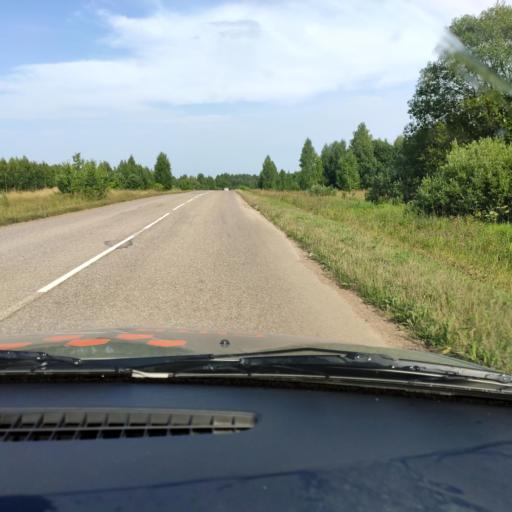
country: RU
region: Bashkortostan
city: Pavlovka
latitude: 55.3837
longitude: 56.4844
